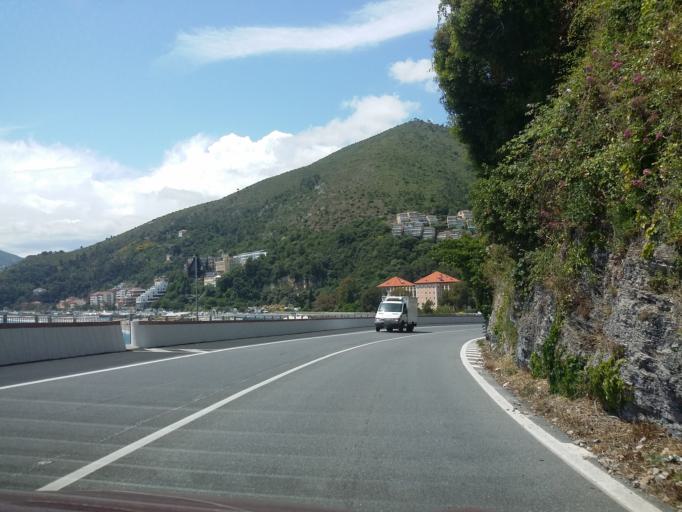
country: IT
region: Liguria
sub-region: Provincia di Savona
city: Bergeggi
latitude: 44.2374
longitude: 8.4405
